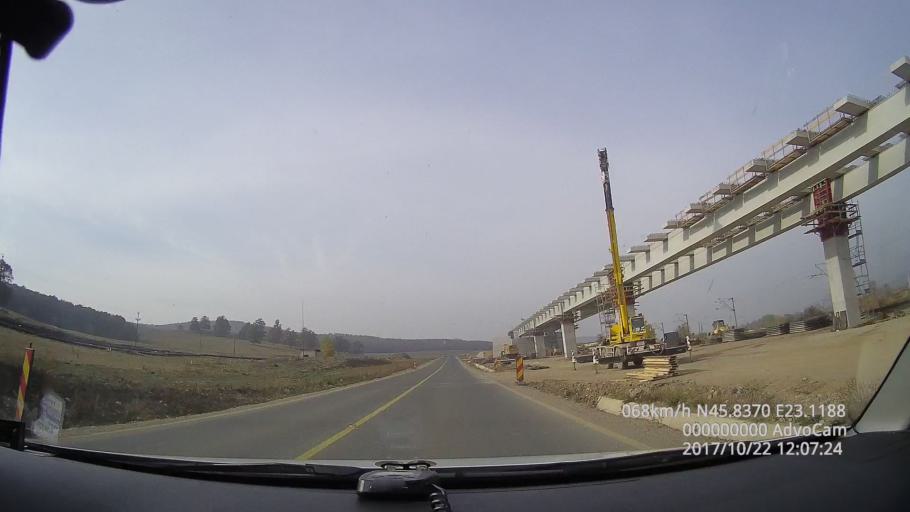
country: RO
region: Timis
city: Timisoara
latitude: 45.7731
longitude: 21.2262
